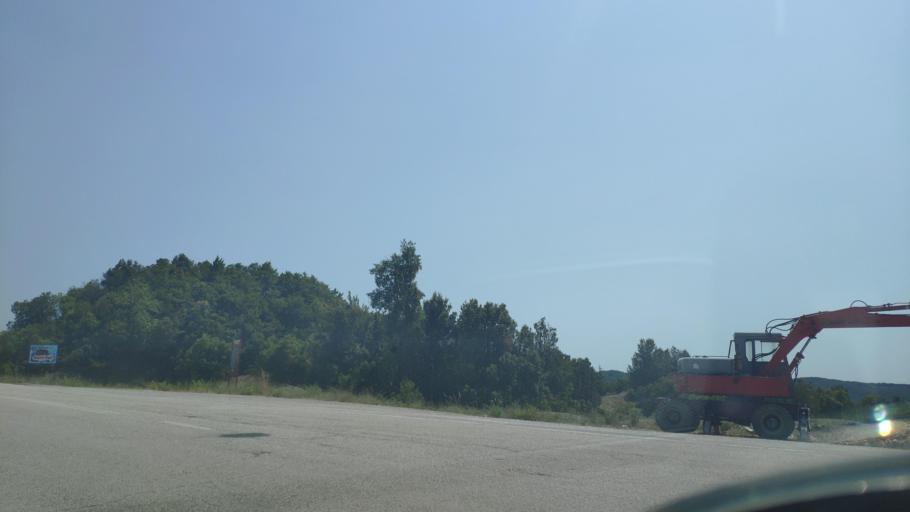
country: GR
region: Epirus
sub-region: Nomos Artas
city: Ano Kalentini
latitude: 39.2147
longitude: 21.1176
